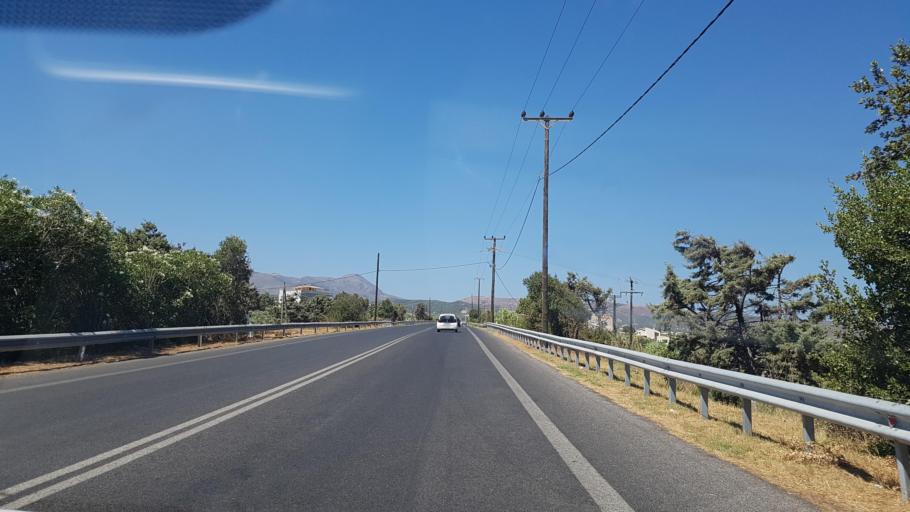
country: GR
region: Crete
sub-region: Nomos Chanias
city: Kissamos
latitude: 35.4997
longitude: 23.7063
